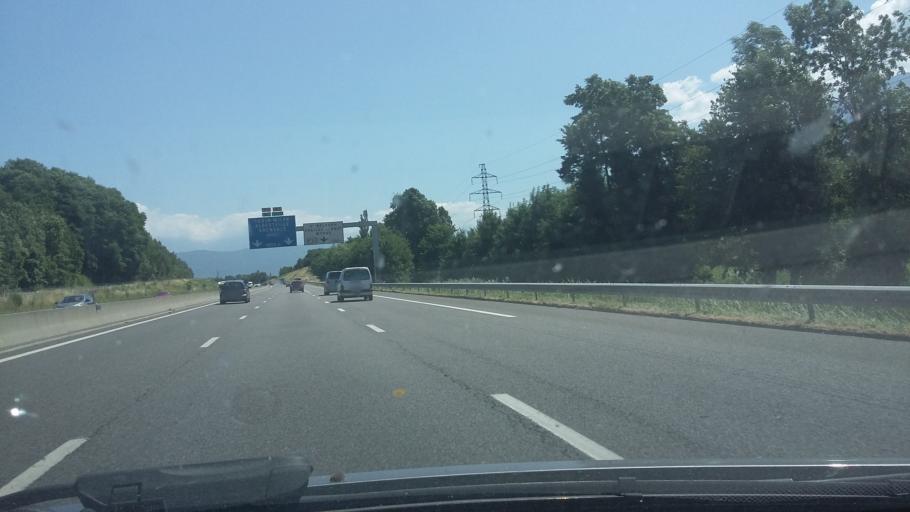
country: FR
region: Rhone-Alpes
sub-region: Departement de la Savoie
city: La Ravoire
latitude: 45.5471
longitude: 5.9600
